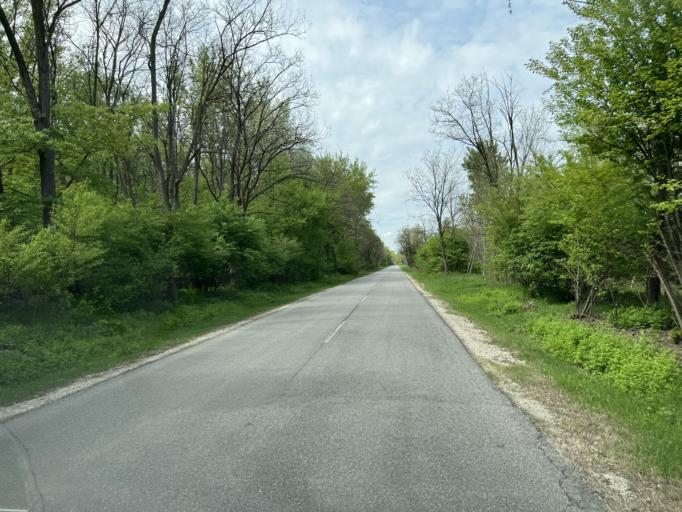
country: HU
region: Pest
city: Csemo
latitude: 47.1534
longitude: 19.6175
